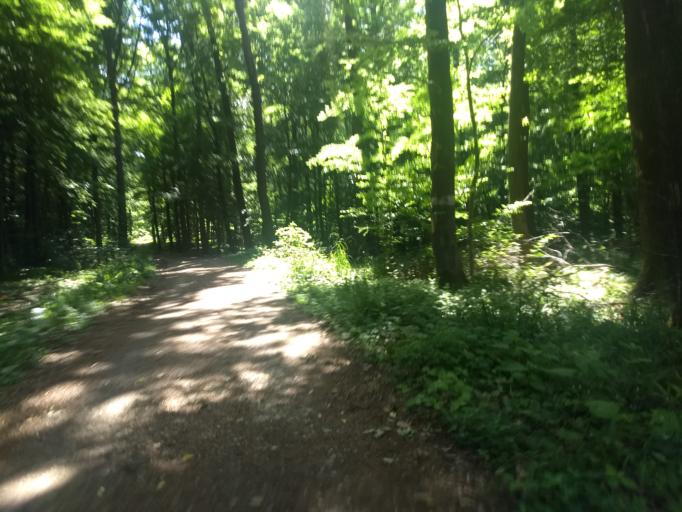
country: AT
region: Lower Austria
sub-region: Politischer Bezirk Wien-Umgebung
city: Gablitz
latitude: 48.2348
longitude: 16.1623
